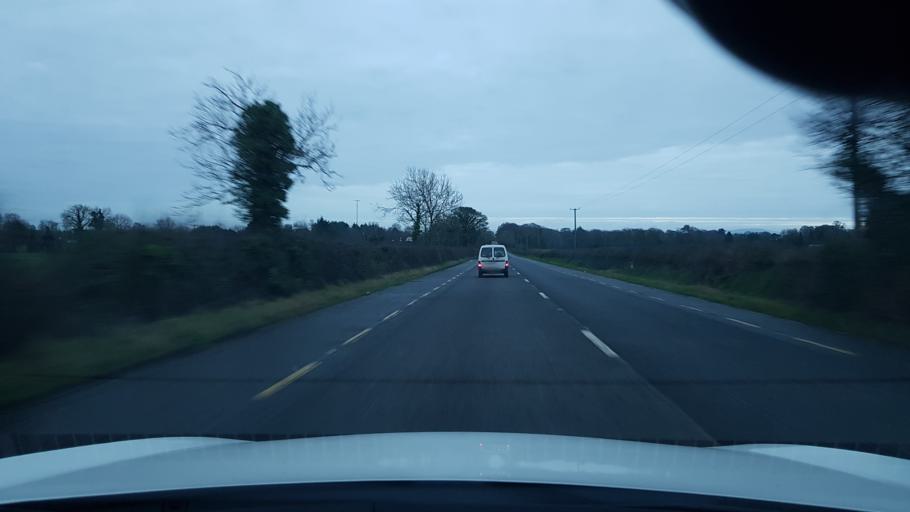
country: IE
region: Leinster
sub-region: An Mhi
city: Ratoath
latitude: 53.4724
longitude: -6.4978
